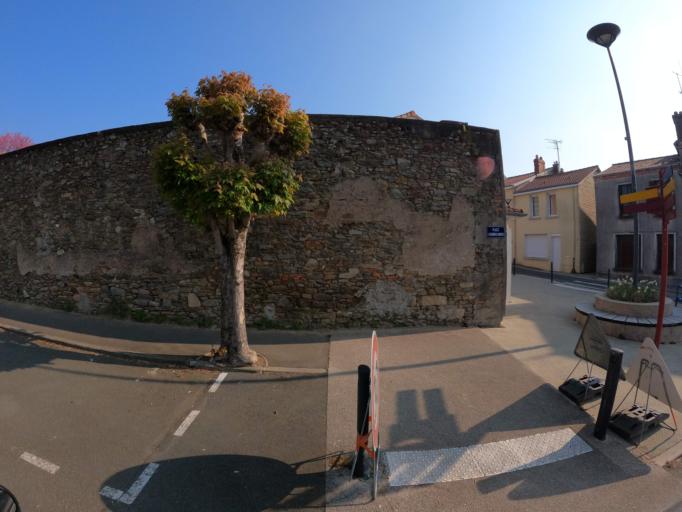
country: FR
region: Pays de la Loire
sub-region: Departement de Maine-et-Loire
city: La Seguiniere
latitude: 47.0628
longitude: -0.9404
